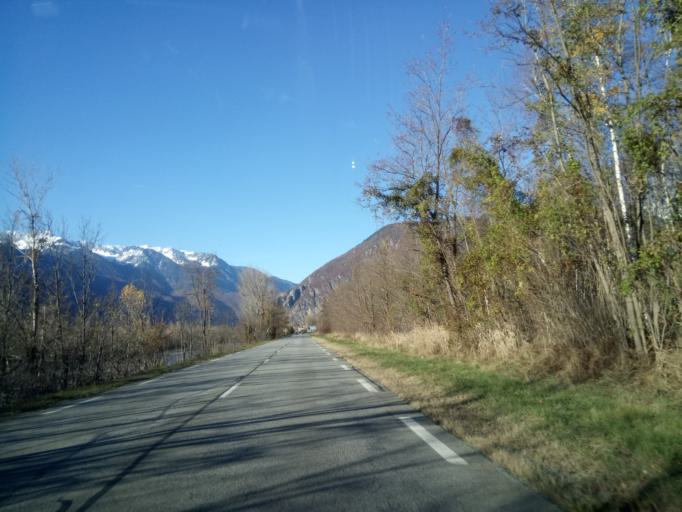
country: FR
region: Rhone-Alpes
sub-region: Departement de la Savoie
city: La Chambre
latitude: 45.3425
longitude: 6.3096
